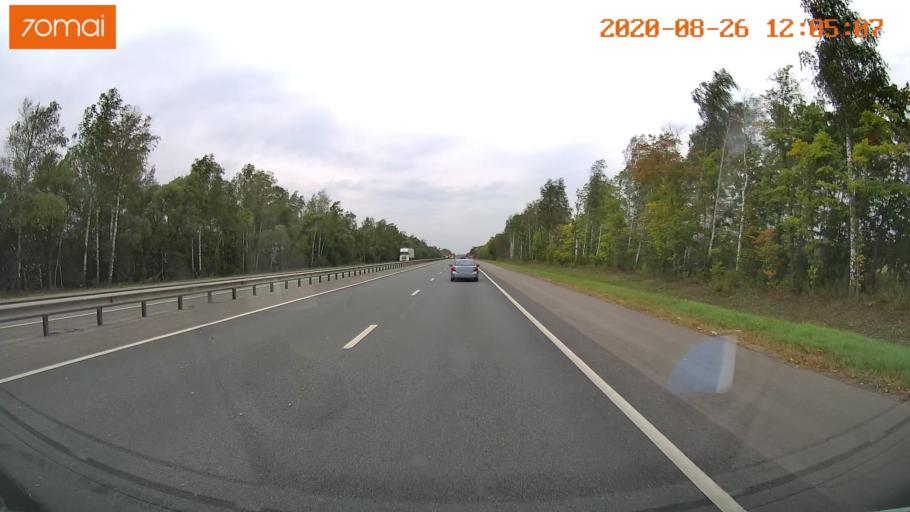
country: RU
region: Rjazan
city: Kiritsy
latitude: 54.3172
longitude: 40.1753
